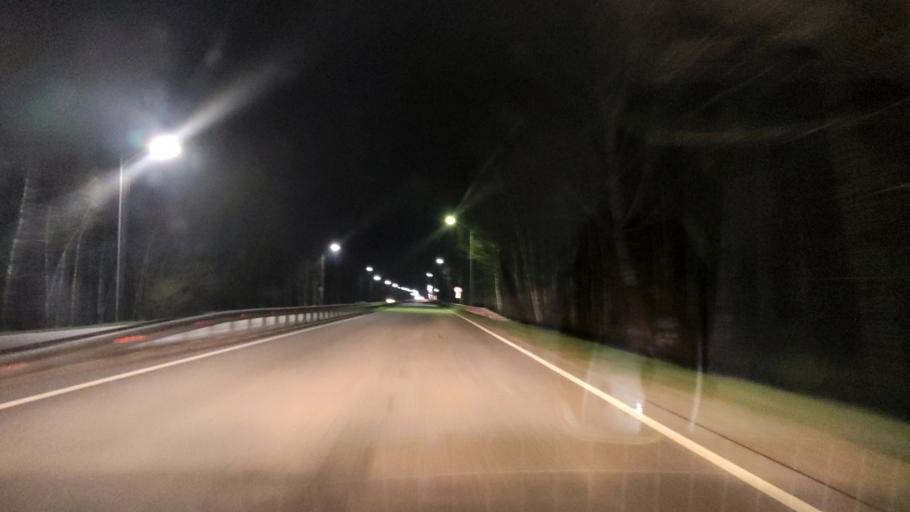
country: RU
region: Belgorod
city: Staryy Oskol
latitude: 51.4101
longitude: 37.8831
